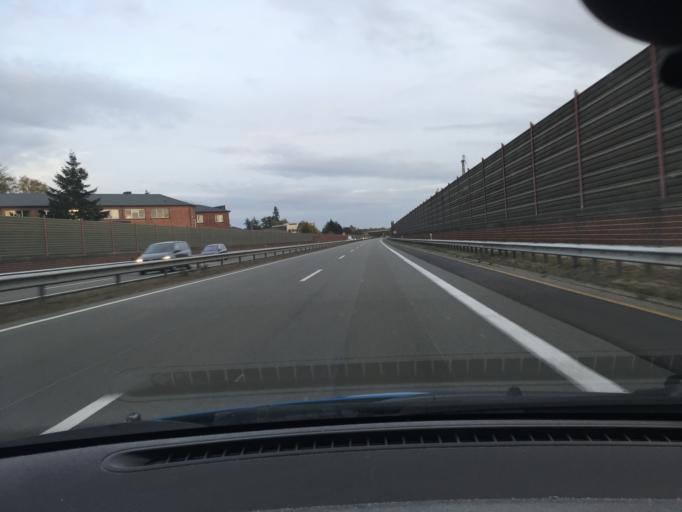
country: DE
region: Lower Saxony
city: Bardowick
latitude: 53.2918
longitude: 10.3690
